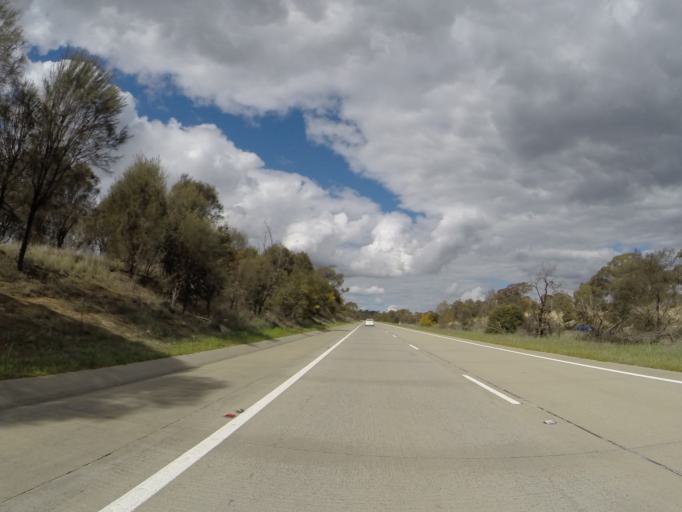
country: AU
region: New South Wales
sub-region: Yass Valley
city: Gundaroo
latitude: -34.7884
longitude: 149.2090
